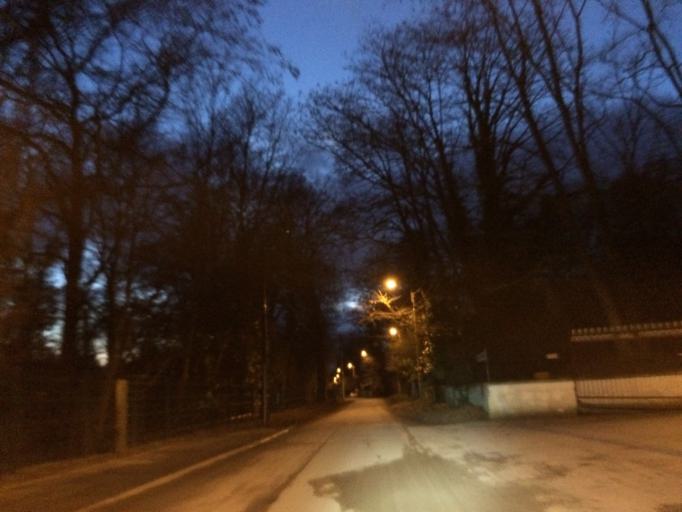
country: FR
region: Picardie
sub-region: Departement de l'Oise
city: Lamorlaye
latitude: 49.1535
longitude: 2.4558
